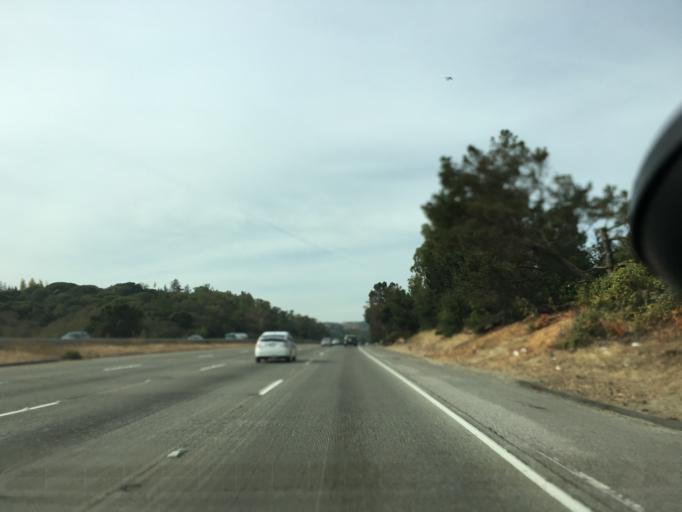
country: US
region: California
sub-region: San Mateo County
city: Woodside
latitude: 37.4302
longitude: -122.2366
